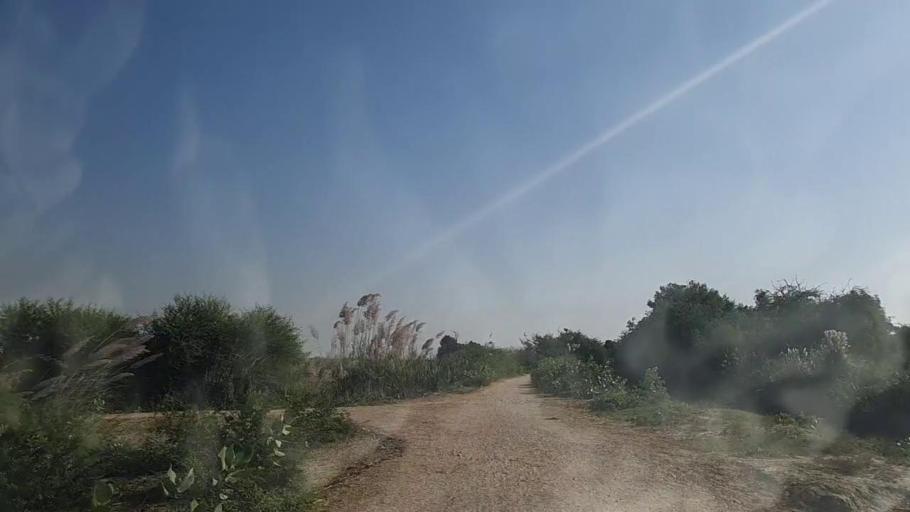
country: PK
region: Sindh
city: Mirpur Batoro
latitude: 24.6345
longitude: 68.1626
